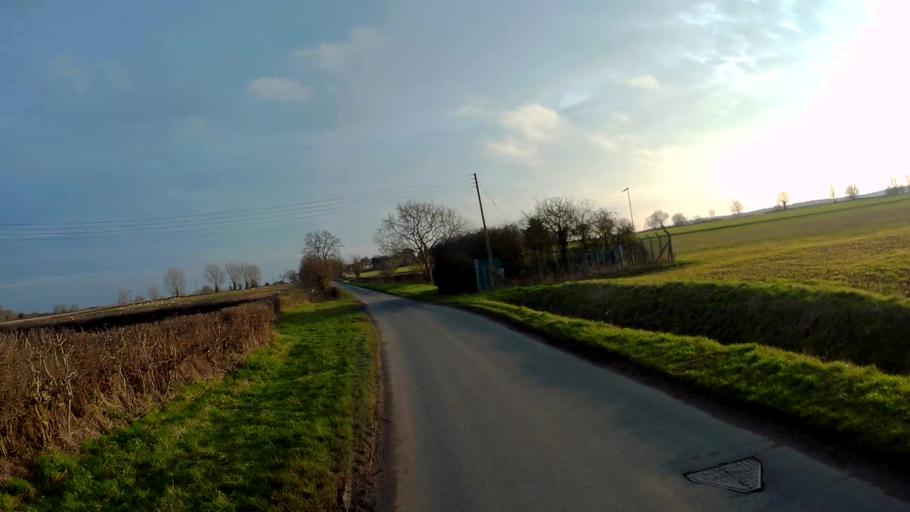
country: GB
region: England
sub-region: Lincolnshire
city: Bourne
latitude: 52.8084
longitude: -0.3971
